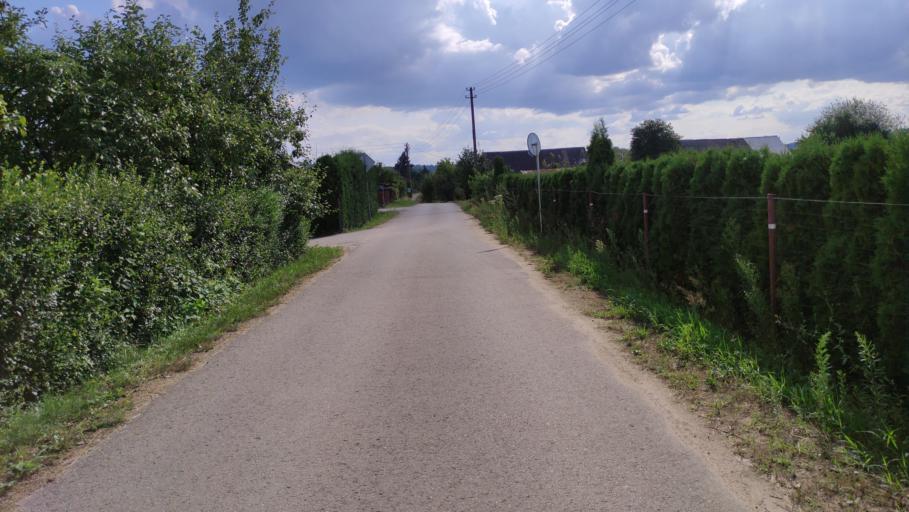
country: LT
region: Alytaus apskritis
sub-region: Alytus
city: Alytus
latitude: 54.4345
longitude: 24.0726
